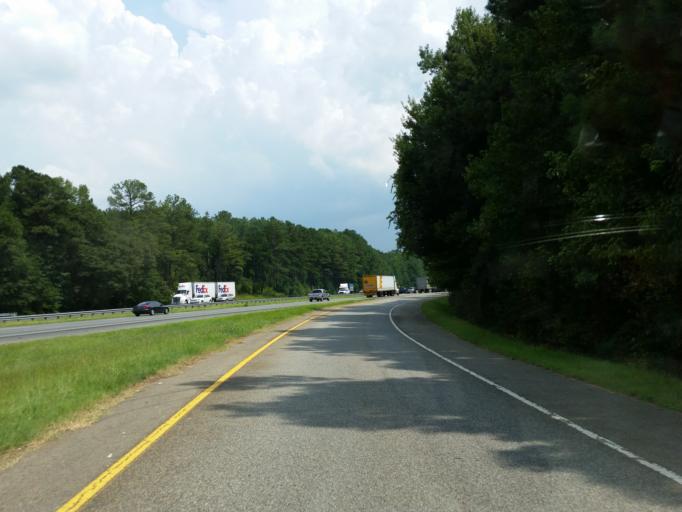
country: US
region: Georgia
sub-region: Monroe County
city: Forsyth
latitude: 33.1100
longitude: -84.0030
